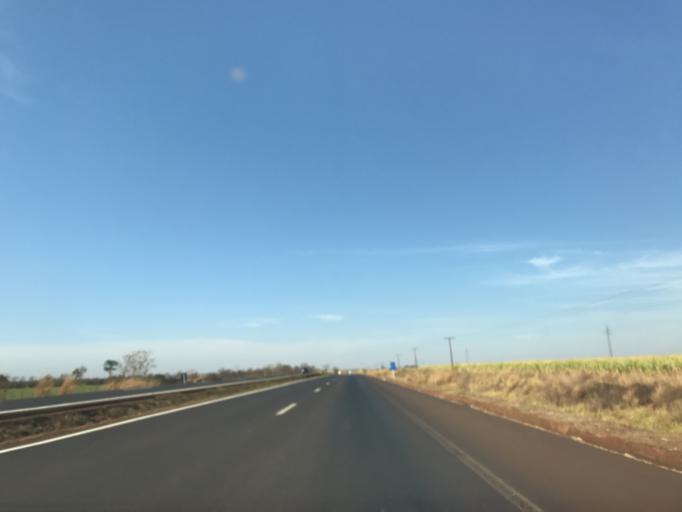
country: BR
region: Goias
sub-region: Itumbiara
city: Itumbiara
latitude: -18.4867
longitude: -49.1887
